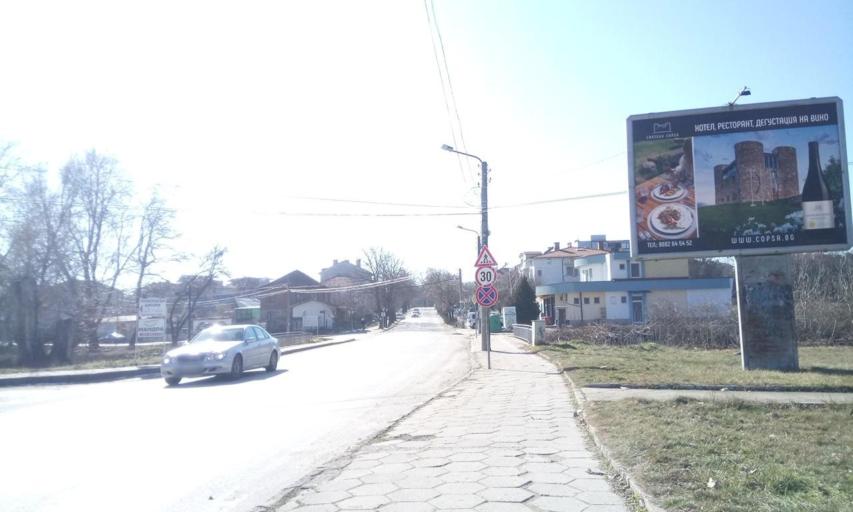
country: BG
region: Plovdiv
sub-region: Obshtina Khisarya
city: Khisarya
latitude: 42.5088
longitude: 24.7139
